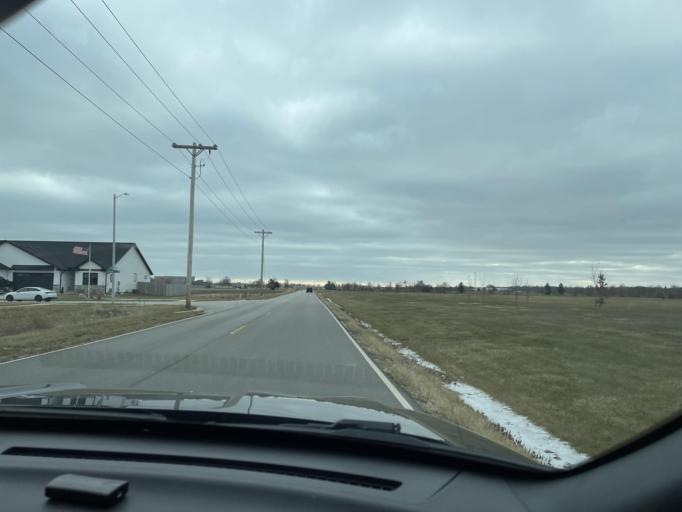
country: US
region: Illinois
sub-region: Sangamon County
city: Jerome
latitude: 39.7628
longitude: -89.7533
